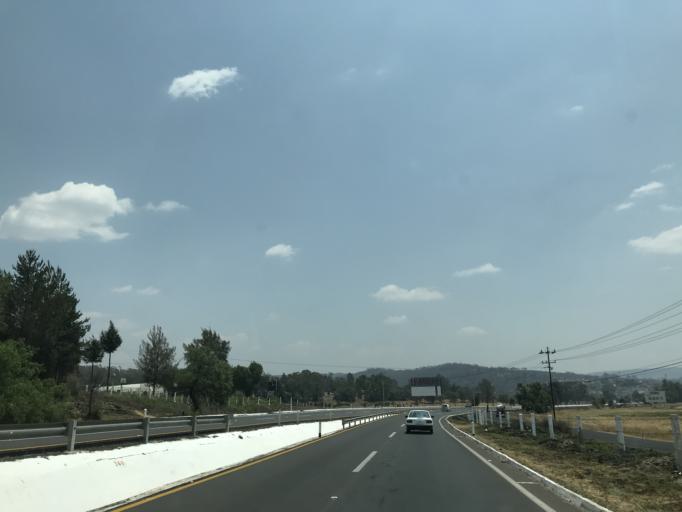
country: MX
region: Tlaxcala
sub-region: Ixtacuixtla de Mariano Matamoros
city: Villa Mariano Matamoros
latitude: 19.3262
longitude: -98.3661
